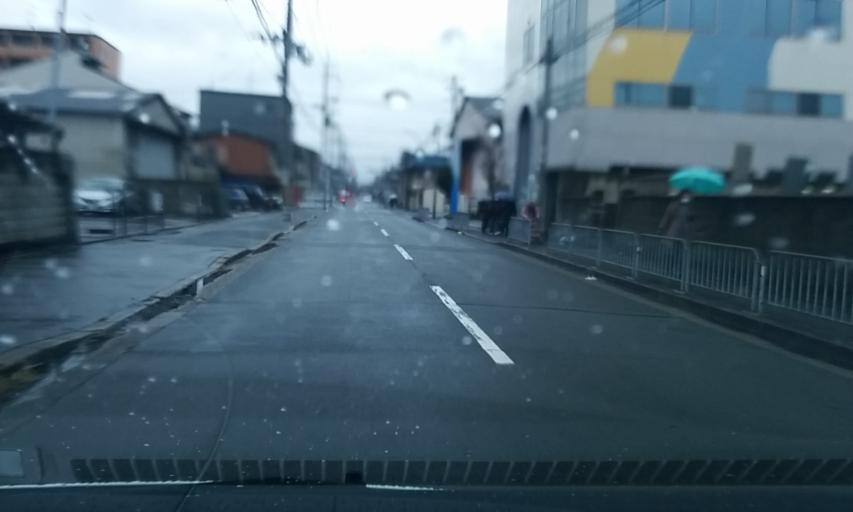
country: JP
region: Kyoto
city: Muko
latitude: 34.9684
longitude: 135.7304
